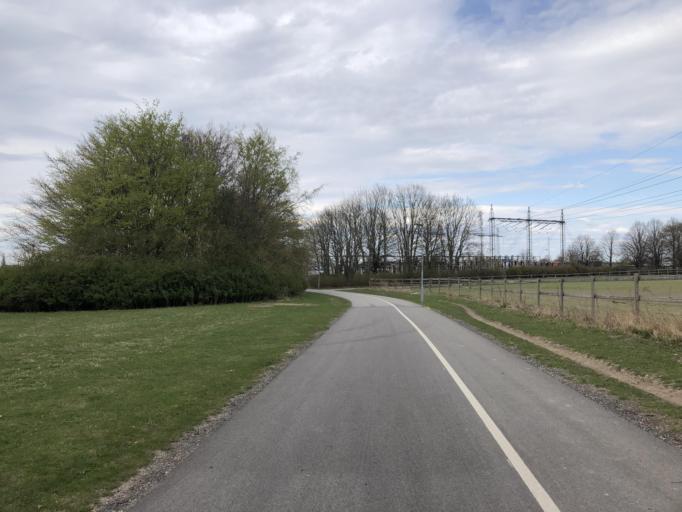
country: SE
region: Skane
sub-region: Malmo
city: Tygelsjo
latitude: 55.5600
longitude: 13.0406
